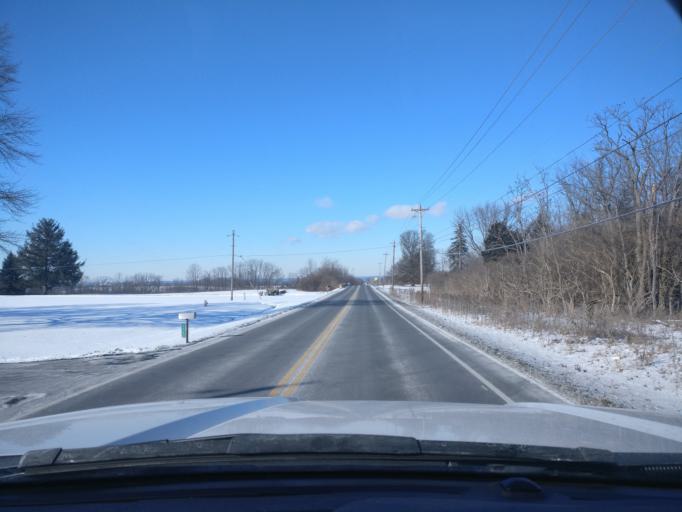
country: US
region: Ohio
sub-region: Warren County
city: Hunter
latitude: 39.5067
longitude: -84.2642
